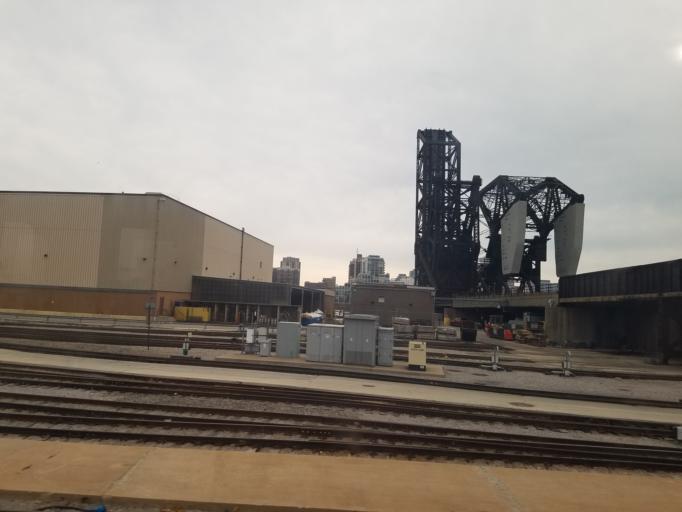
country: US
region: Illinois
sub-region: Cook County
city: Chicago
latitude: 41.8609
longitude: -87.6367
